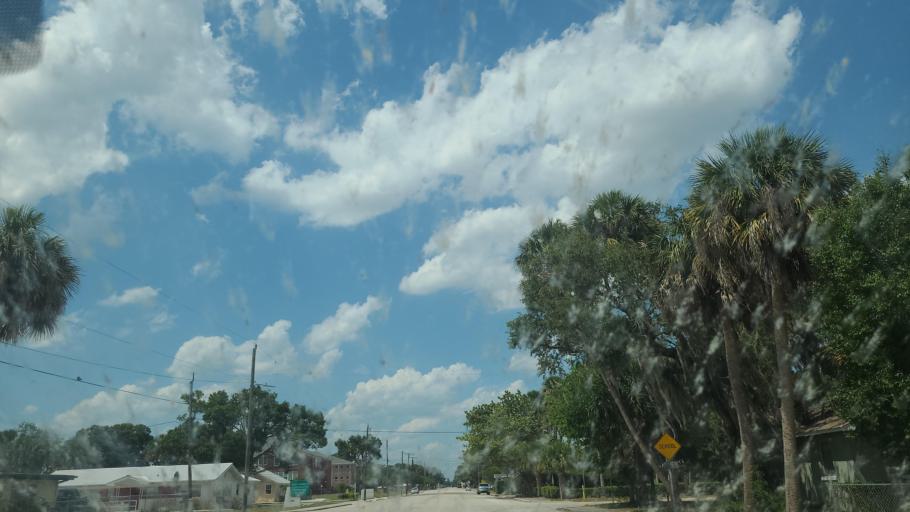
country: US
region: Florida
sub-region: Okeechobee County
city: Okeechobee
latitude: 27.2346
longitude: -80.8311
